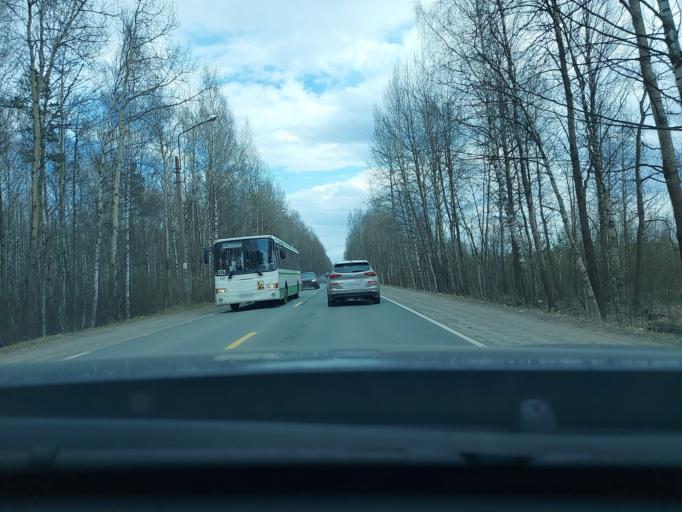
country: RU
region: St.-Petersburg
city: Sapernyy
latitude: 59.7663
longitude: 30.7321
